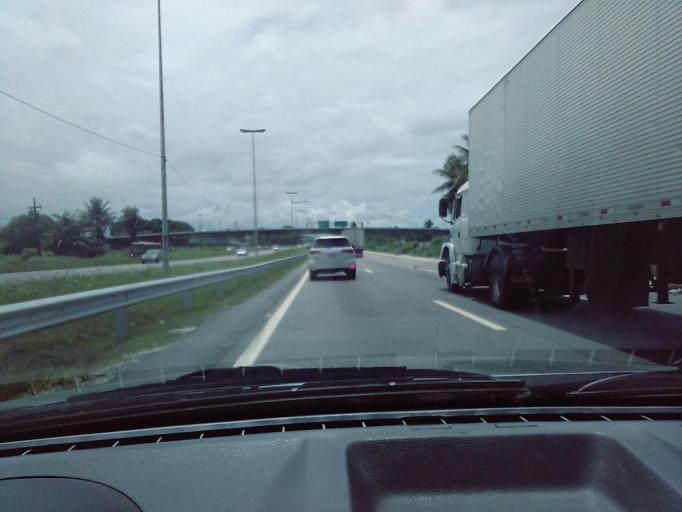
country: BR
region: Pernambuco
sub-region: Recife
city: Recife
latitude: -8.0771
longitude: -34.9425
